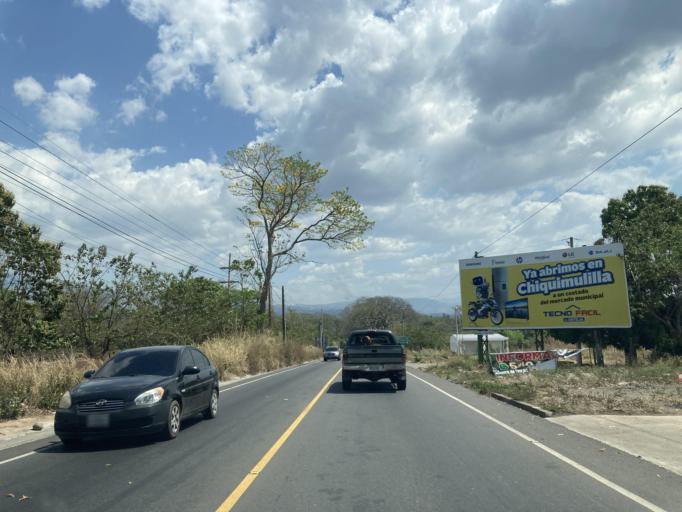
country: GT
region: Santa Rosa
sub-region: Municipio de Chiquimulilla
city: Chiquimulilla
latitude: 14.0680
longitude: -90.3901
